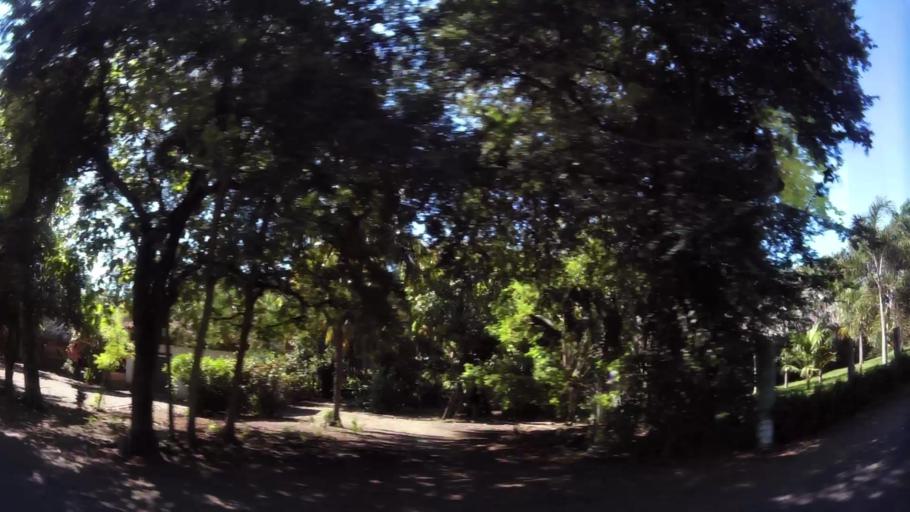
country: GT
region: Santa Rosa
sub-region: Municipio de Taxisco
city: Taxisco
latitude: 13.9078
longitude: -90.5183
